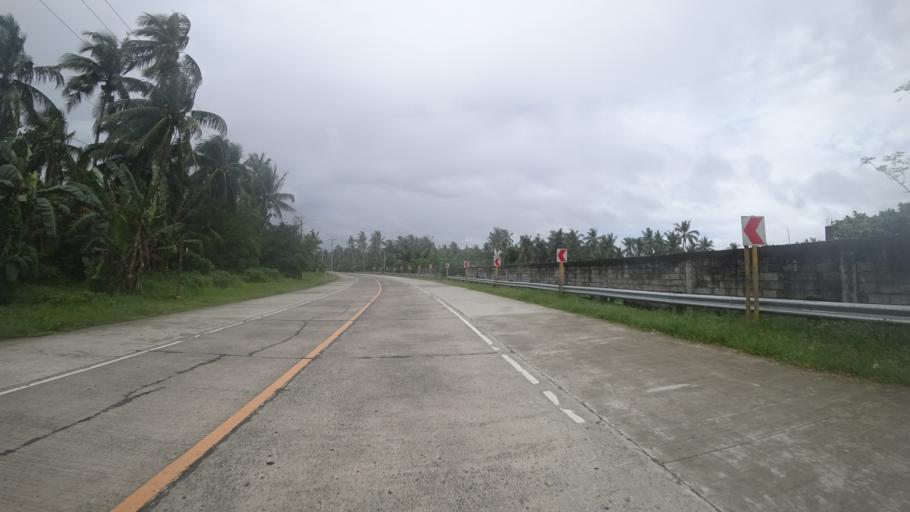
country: PH
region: Eastern Visayas
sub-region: Province of Leyte
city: MacArthur
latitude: 10.8510
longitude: 124.9955
